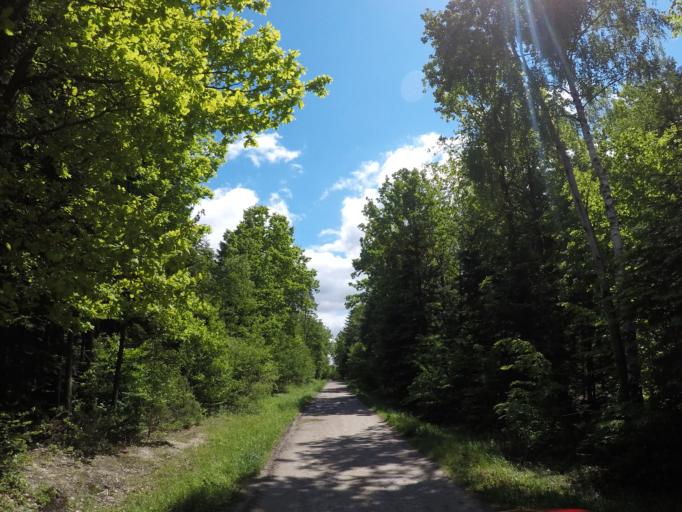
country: PL
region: Swietokrzyskie
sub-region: Powiat kielecki
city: Domaszowice
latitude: 50.9111
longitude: 20.6585
